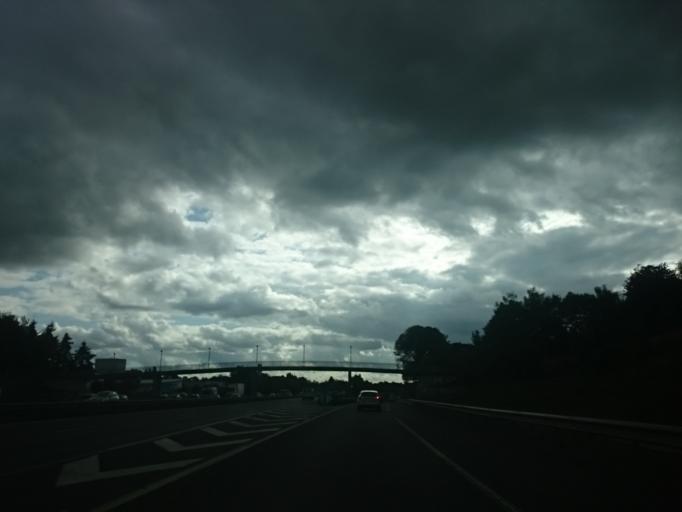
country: FR
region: Brittany
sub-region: Departement d'Ille-et-Vilaine
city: Montgermont
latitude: 48.1299
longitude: -1.7108
